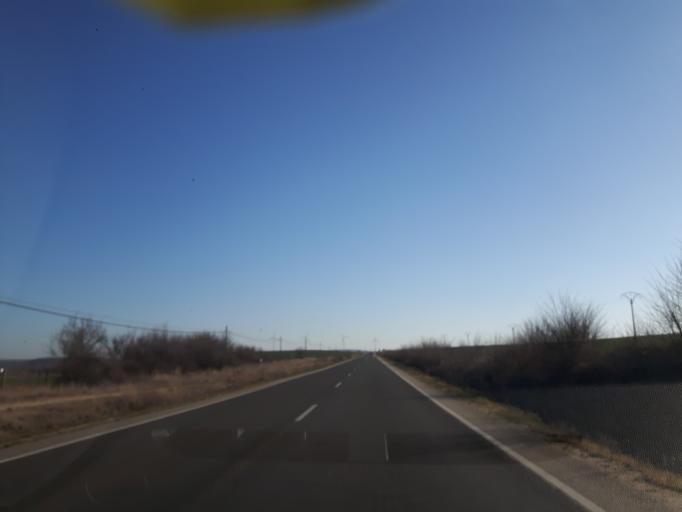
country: ES
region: Castille and Leon
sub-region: Provincia de Salamanca
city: Garcihernandez
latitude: 40.8464
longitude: -5.4601
